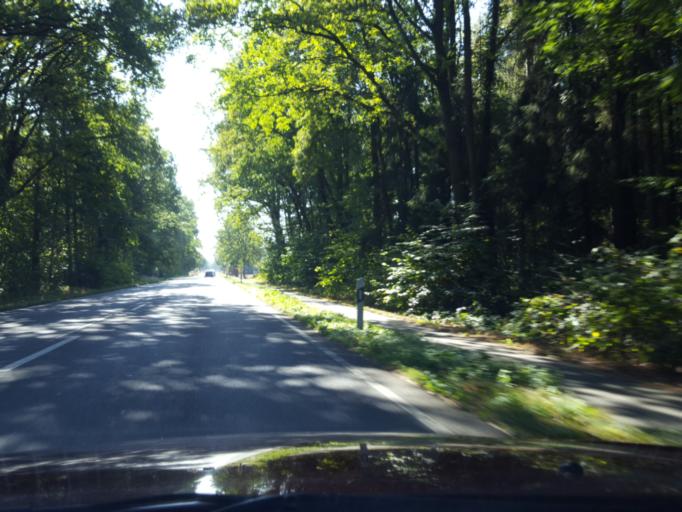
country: DE
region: Lower Saxony
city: Eystrup
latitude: 52.8088
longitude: 9.2032
